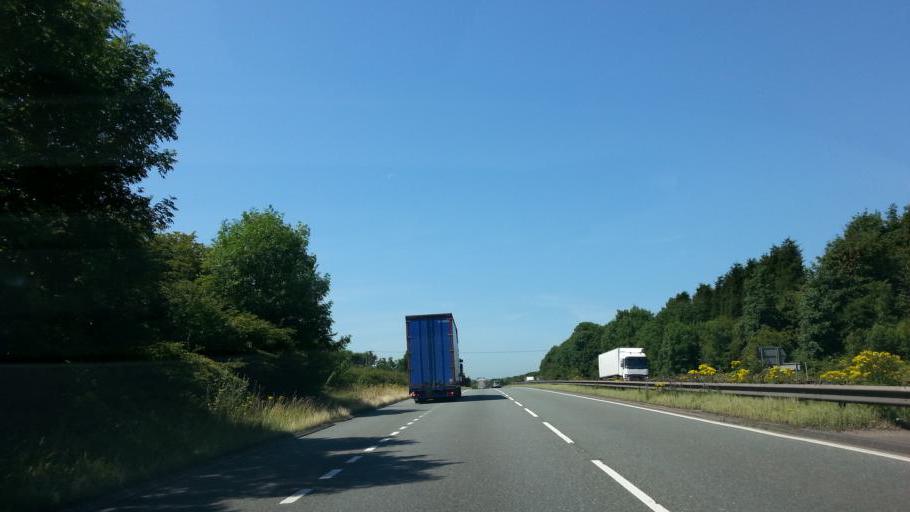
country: GB
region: England
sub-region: Derbyshire
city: Blackwell
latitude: 53.0934
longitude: -1.3479
